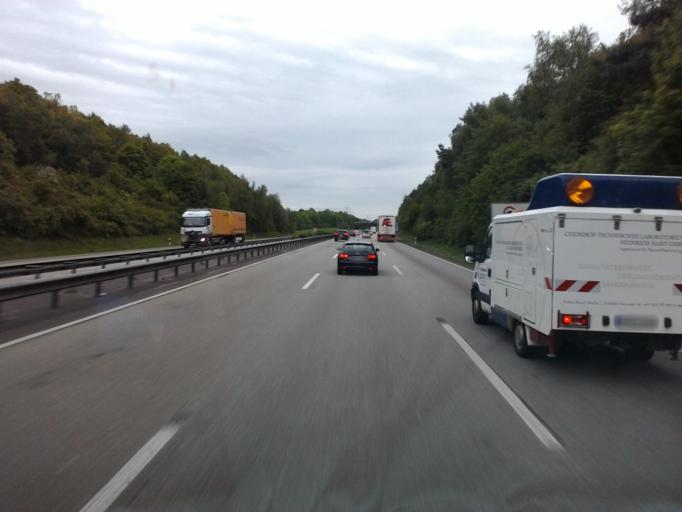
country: DE
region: Rheinland-Pfalz
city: Konigsfeld
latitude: 50.5307
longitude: 7.1813
